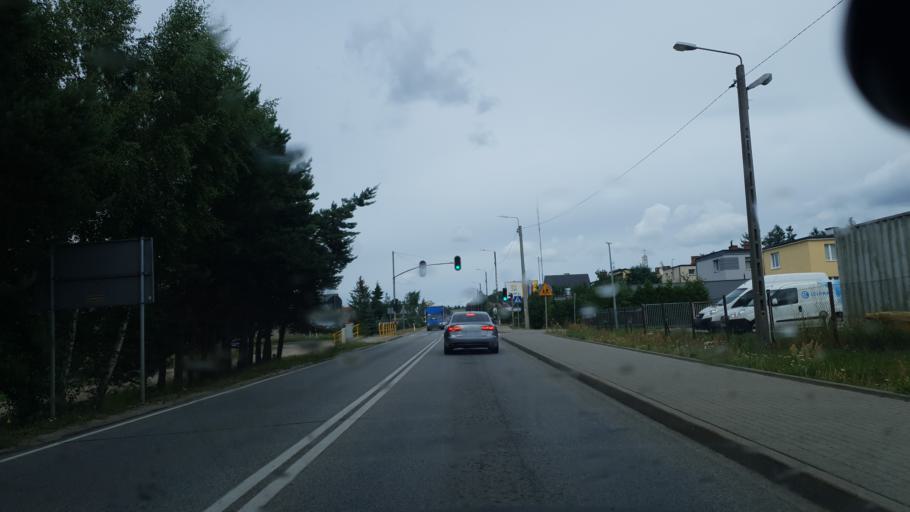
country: PL
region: Pomeranian Voivodeship
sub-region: Powiat kartuski
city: Chwaszczyno
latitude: 54.4399
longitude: 18.4141
